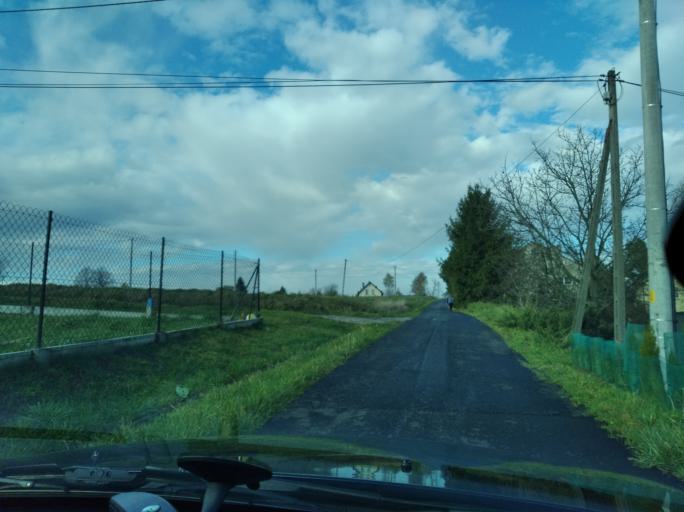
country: PL
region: Subcarpathian Voivodeship
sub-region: Powiat debicki
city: Debica
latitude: 50.0268
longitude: 21.4650
